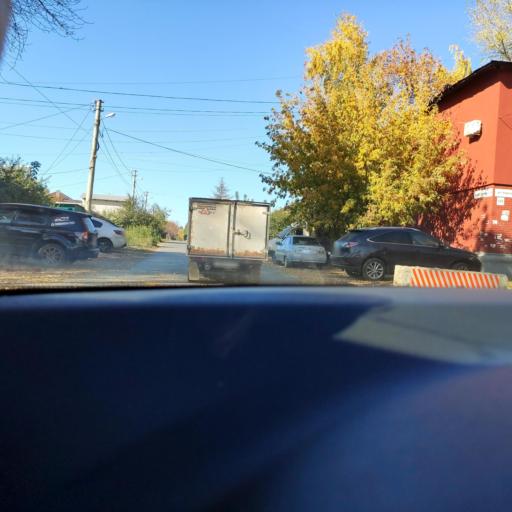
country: RU
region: Samara
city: Samara
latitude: 53.2308
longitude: 50.2377
